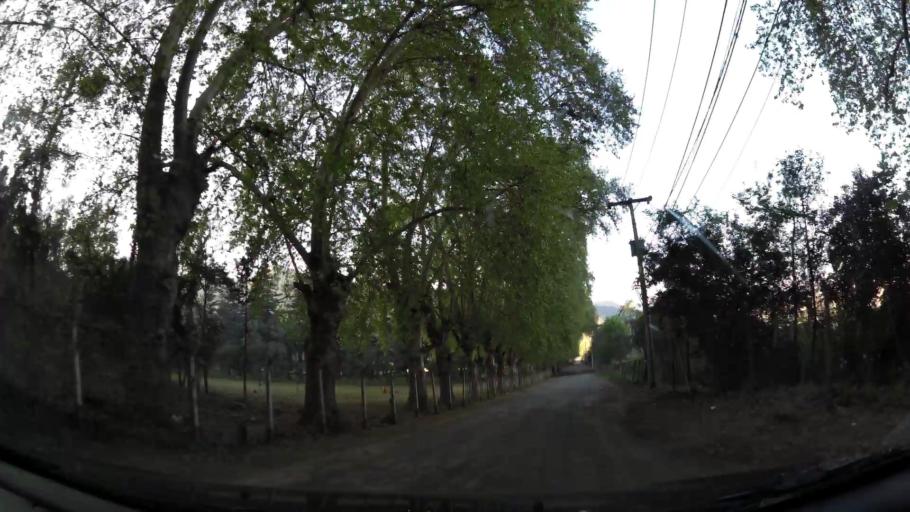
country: CL
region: Santiago Metropolitan
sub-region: Provincia de Santiago
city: Santiago
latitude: -33.3850
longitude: -70.6112
